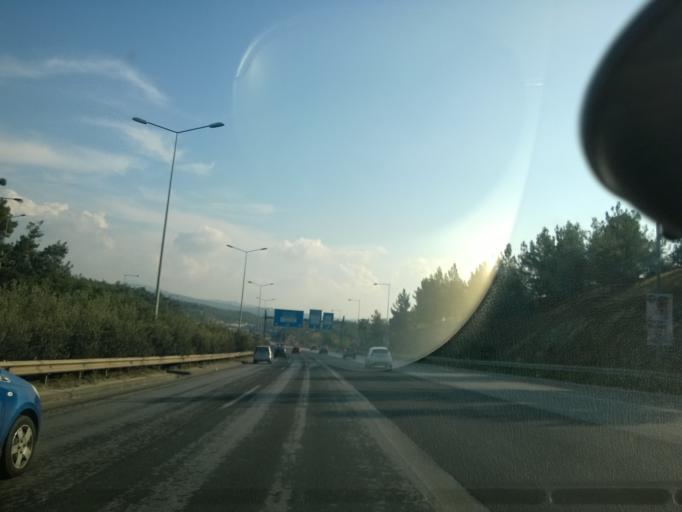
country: GR
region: Central Macedonia
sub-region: Nomos Thessalonikis
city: Triandria
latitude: 40.6310
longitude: 22.9745
